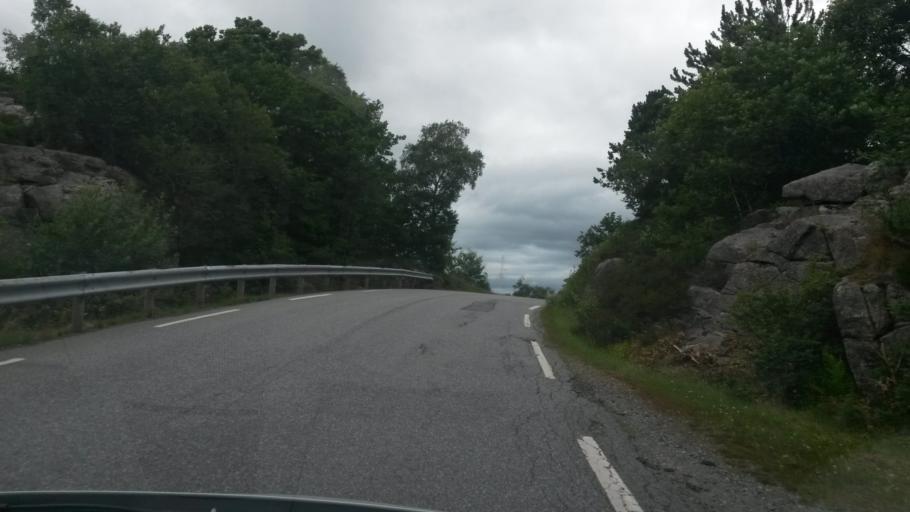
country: NO
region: Rogaland
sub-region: Sandnes
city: Sandnes
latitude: 58.8947
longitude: 5.7746
